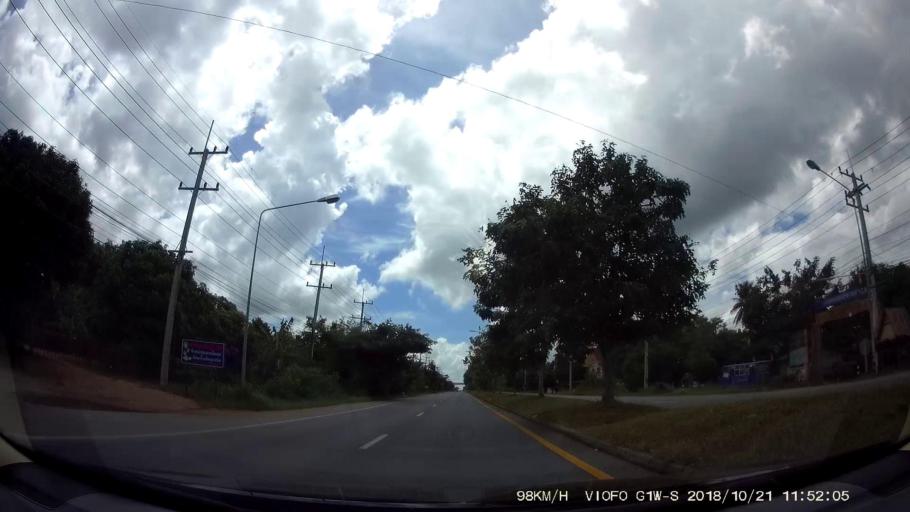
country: TH
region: Chaiyaphum
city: Chatturat
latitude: 15.6144
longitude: 101.9137
